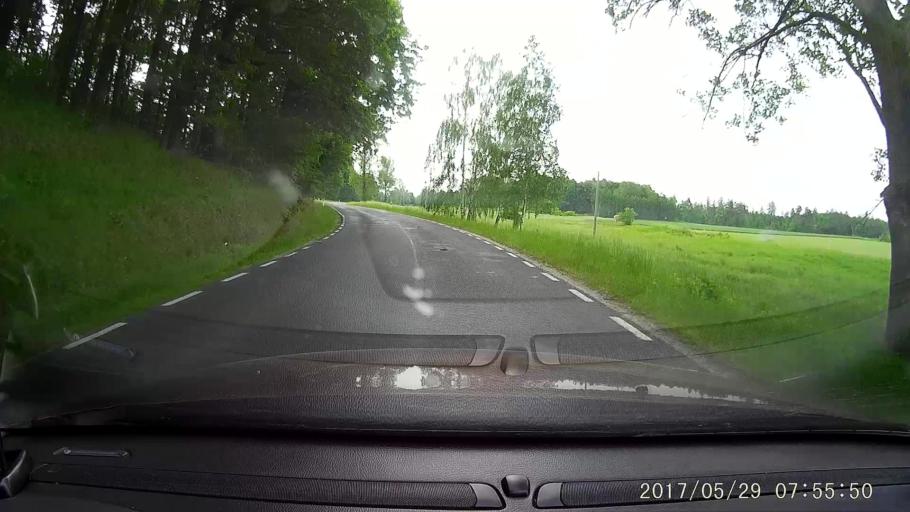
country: PL
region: Lower Silesian Voivodeship
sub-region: Powiat zlotoryjski
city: Olszanica
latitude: 51.2105
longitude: 15.7605
